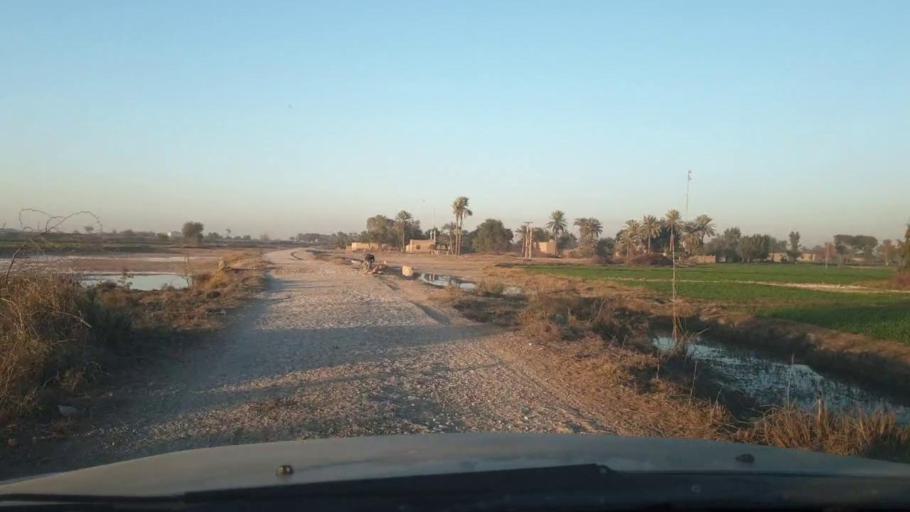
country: PK
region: Sindh
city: Pano Aqil
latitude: 27.9139
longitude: 69.1939
